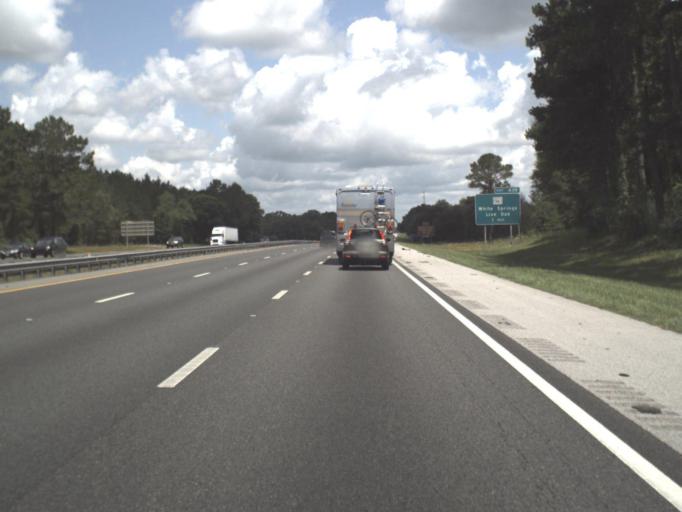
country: US
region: Florida
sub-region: Suwannee County
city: Wellborn
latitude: 30.3066
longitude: -82.7954
